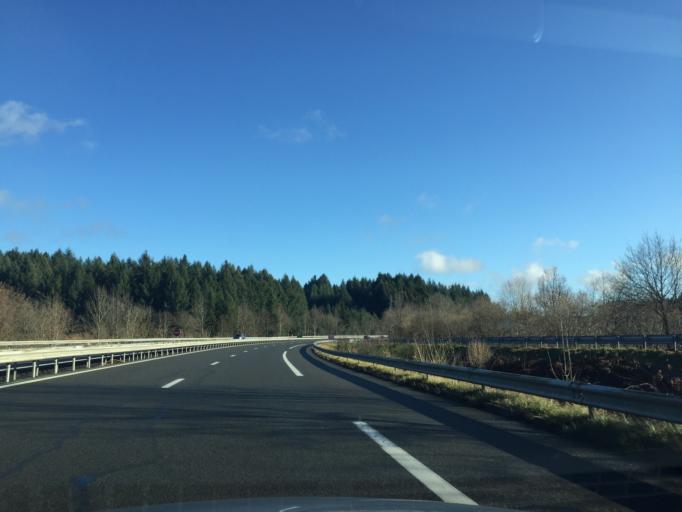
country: FR
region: Auvergne
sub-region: Departement du Puy-de-Dome
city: Celles-sur-Durolle
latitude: 45.8816
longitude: 3.6239
